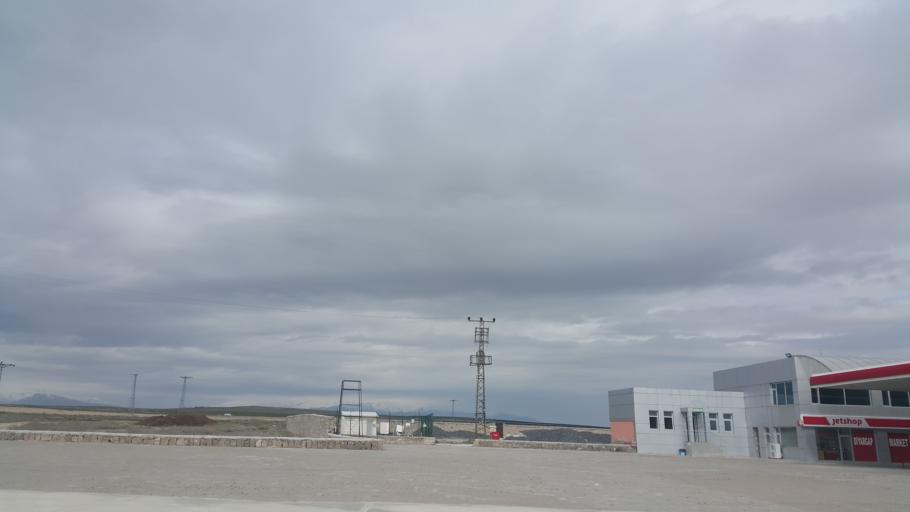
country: TR
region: Nigde
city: Altunhisar
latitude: 37.8315
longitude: 34.1920
